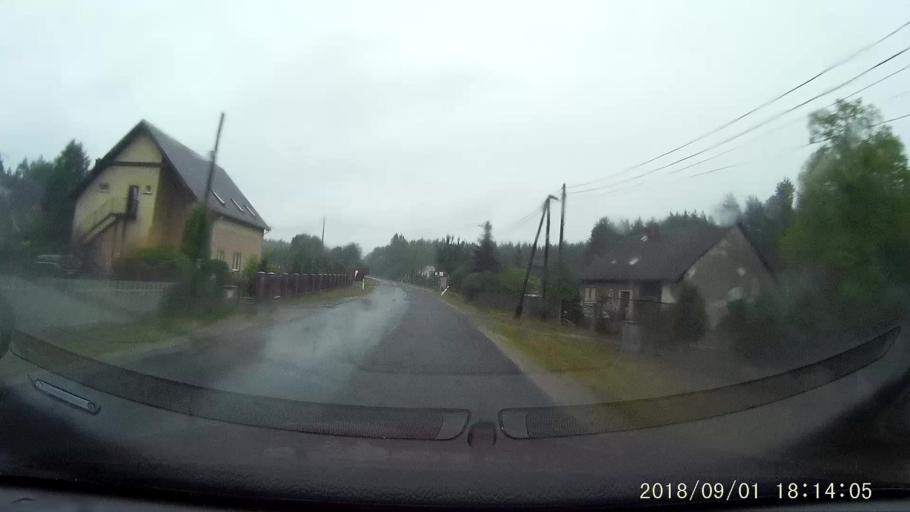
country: PL
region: Lower Silesian Voivodeship
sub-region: Powiat zgorzelecki
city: Piensk
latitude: 51.2969
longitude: 15.0587
